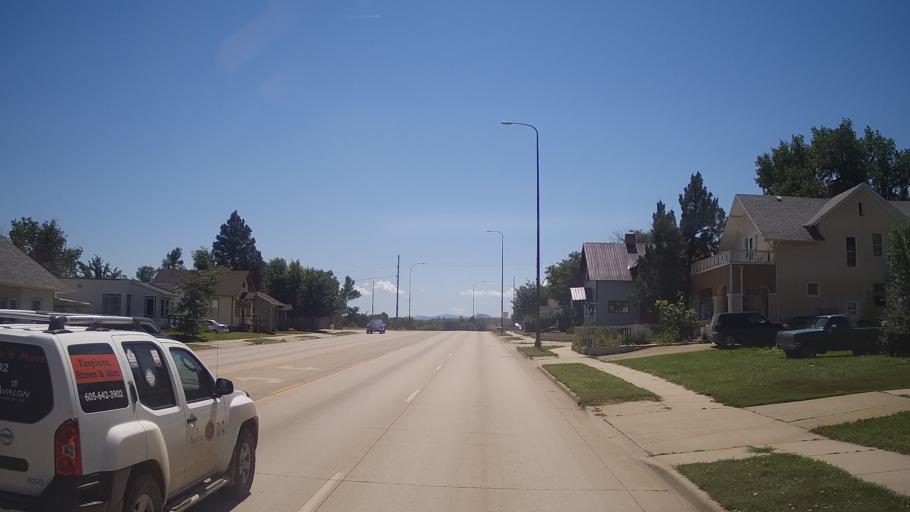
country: US
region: South Dakota
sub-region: Butte County
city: Belle Fourche
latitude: 44.6661
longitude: -103.8537
